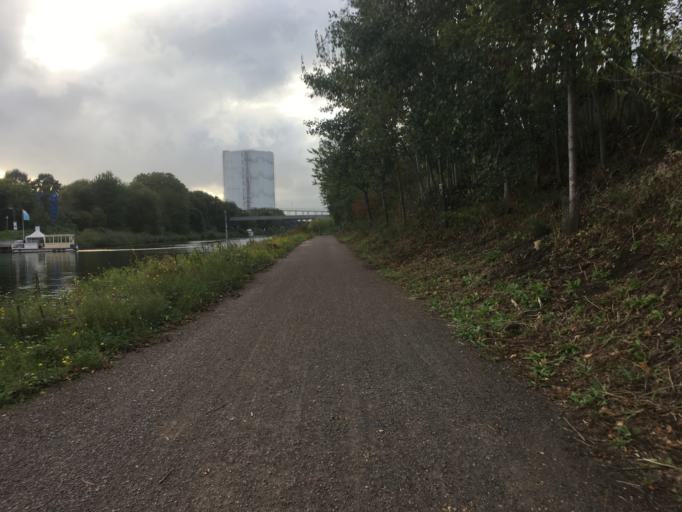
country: DE
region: North Rhine-Westphalia
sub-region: Regierungsbezirk Dusseldorf
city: Oberhausen
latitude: 51.4954
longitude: 6.8829
